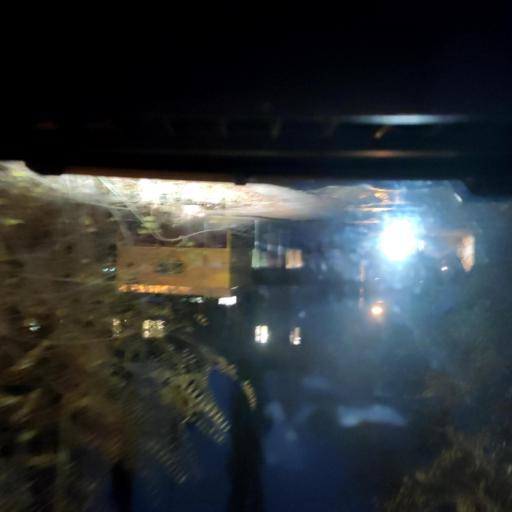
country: RU
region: Voronezj
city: Maslovka
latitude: 51.6139
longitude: 39.2437
